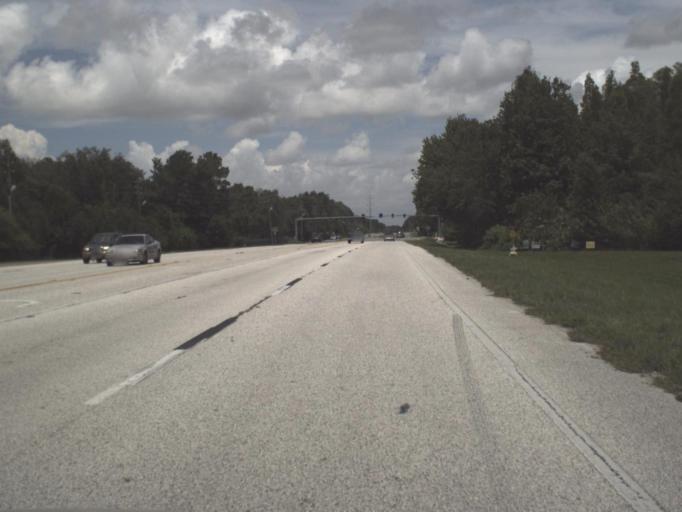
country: US
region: Florida
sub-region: Pasco County
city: Trinity
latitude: 28.1718
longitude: -82.6989
